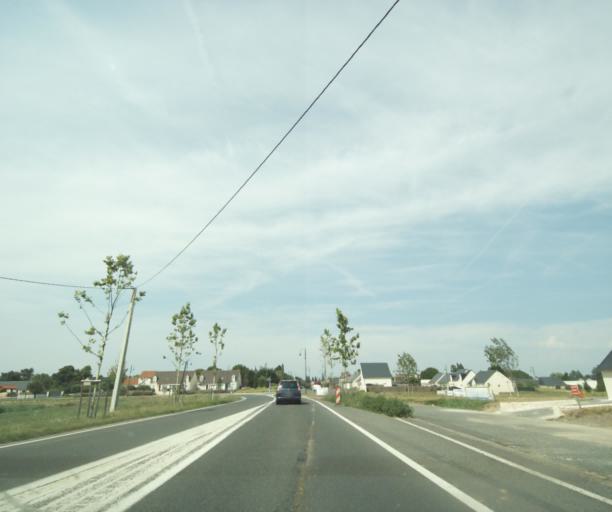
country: FR
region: Centre
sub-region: Departement d'Indre-et-Loire
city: Sorigny
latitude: 47.2369
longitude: 0.6912
